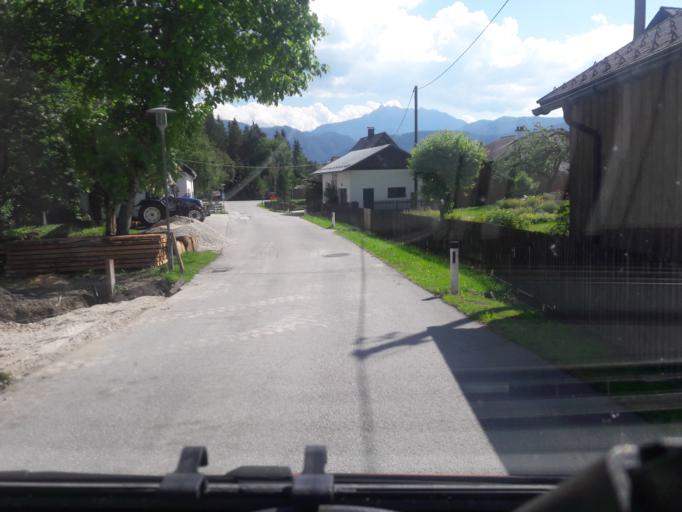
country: AT
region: Styria
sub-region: Politischer Bezirk Liezen
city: Tauplitz
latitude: 47.5531
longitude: 13.9506
